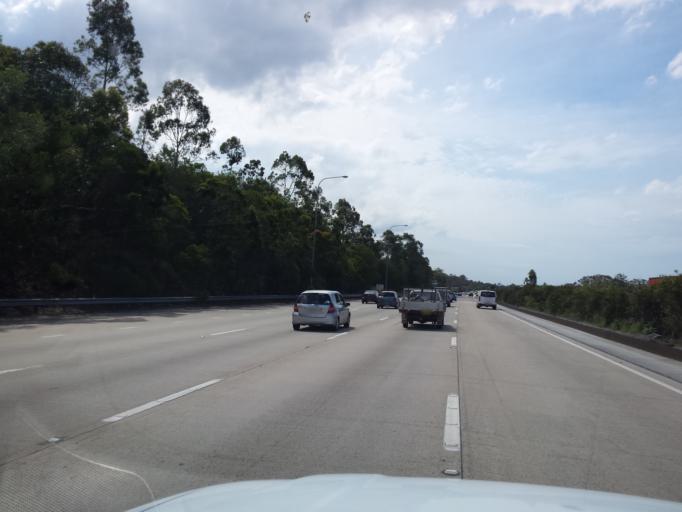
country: AU
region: Queensland
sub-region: Gold Coast
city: Nerang
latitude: -27.9470
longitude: 153.3402
